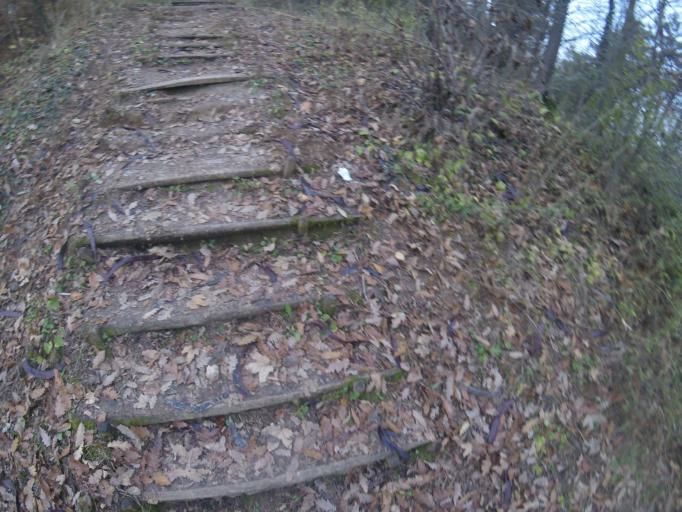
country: HU
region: Tolna
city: Szekszard
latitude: 46.3474
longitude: 18.6944
